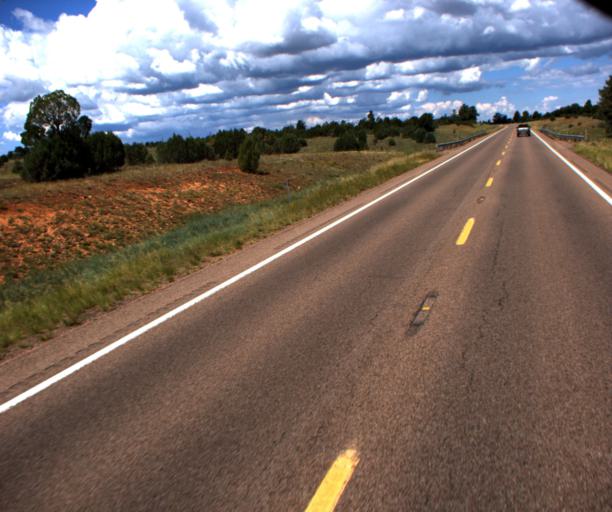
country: US
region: Arizona
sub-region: Navajo County
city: Heber-Overgaard
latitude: 34.3765
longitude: -110.4651
